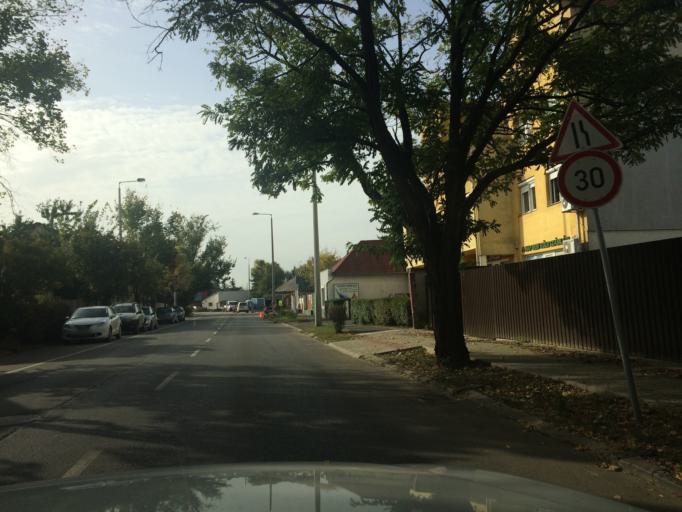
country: HU
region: Szabolcs-Szatmar-Bereg
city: Nyiregyhaza
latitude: 47.9478
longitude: 21.7193
